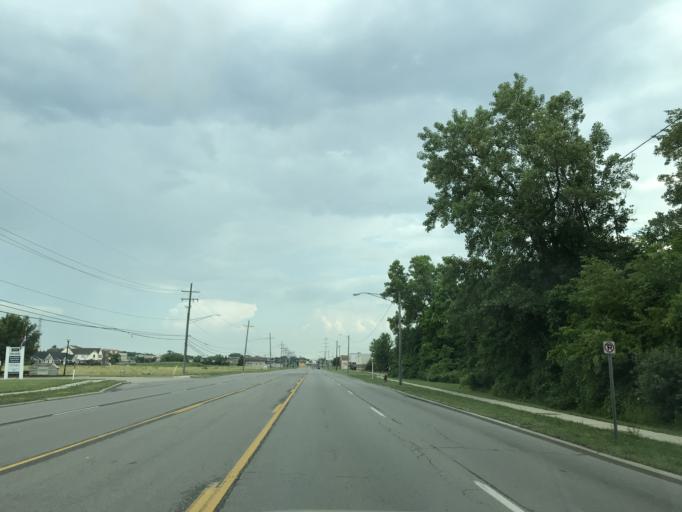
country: US
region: Michigan
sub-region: Wayne County
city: Southgate
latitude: 42.2181
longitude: -83.2294
